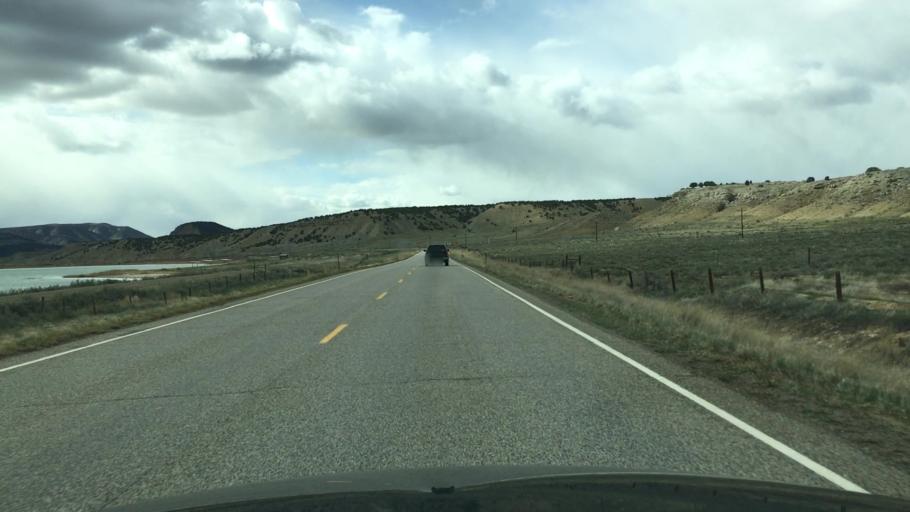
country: US
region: Colorado
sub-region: Rio Blanco County
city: Meeker
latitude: 40.0890
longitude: -108.2034
